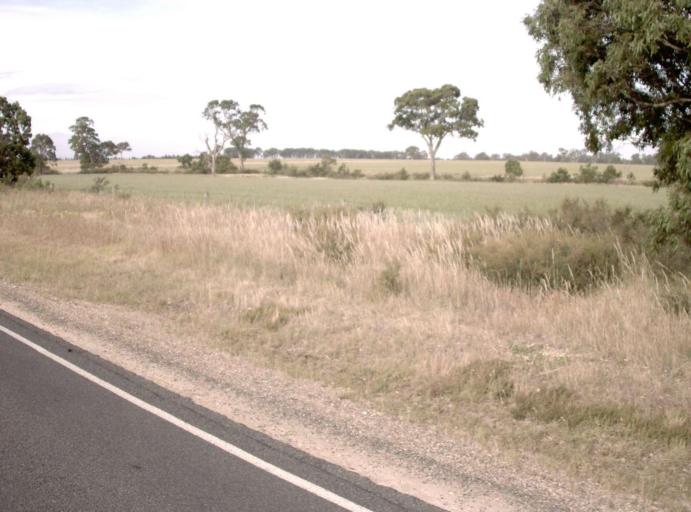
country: AU
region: Victoria
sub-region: Wellington
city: Heyfield
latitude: -38.0517
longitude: 146.6636
